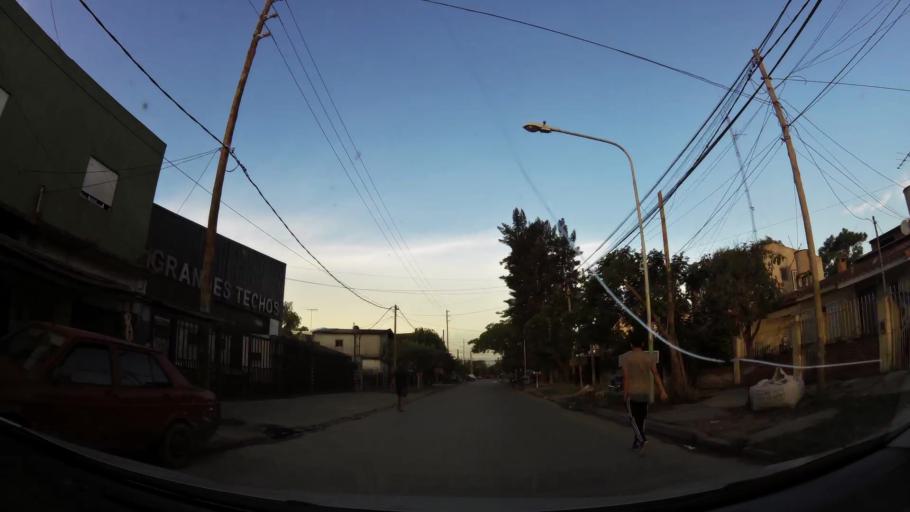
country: AR
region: Buenos Aires
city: Santa Catalina - Dique Lujan
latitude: -34.4356
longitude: -58.6700
